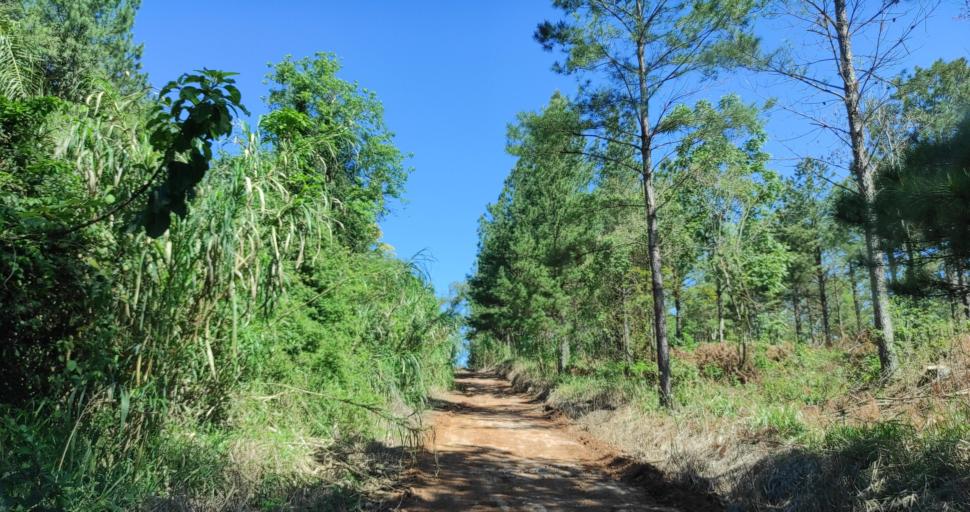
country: AR
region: Misiones
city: Ruiz de Montoya
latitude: -26.9468
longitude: -54.9808
